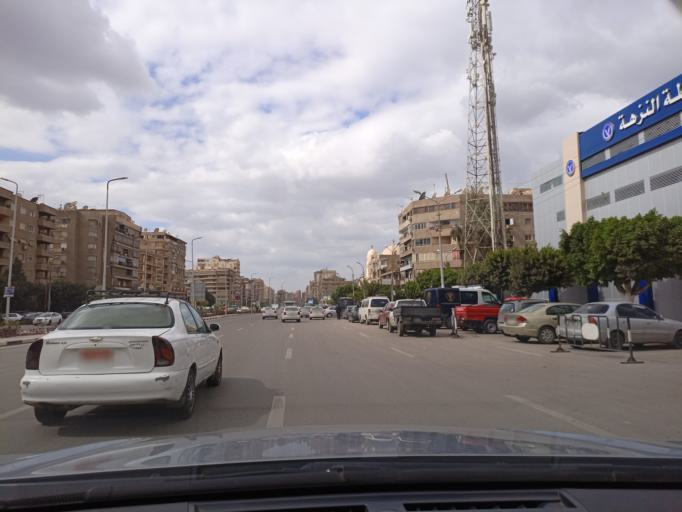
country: EG
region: Muhafazat al Qahirah
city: Cairo
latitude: 30.1069
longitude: 31.3409
